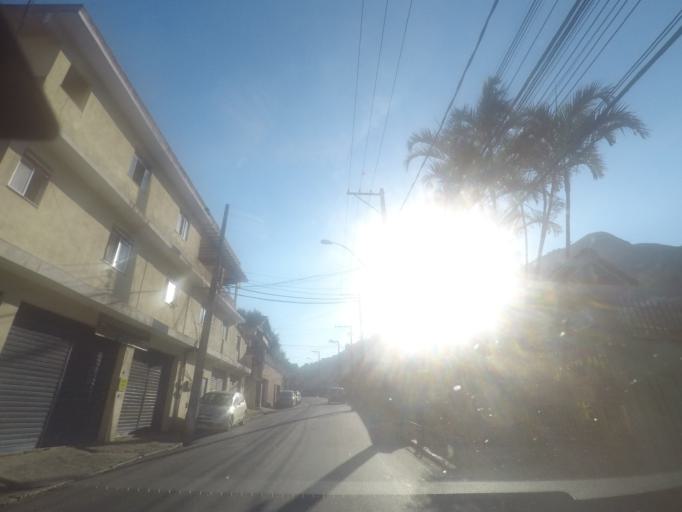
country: BR
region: Rio de Janeiro
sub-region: Petropolis
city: Petropolis
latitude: -22.4913
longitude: -43.1563
